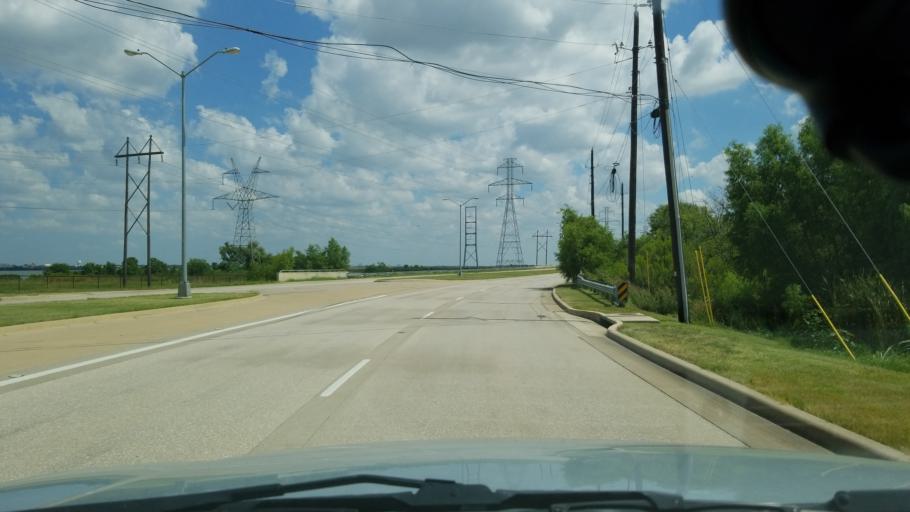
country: US
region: Texas
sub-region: Dallas County
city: Grand Prairie
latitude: 32.7138
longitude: -96.9514
